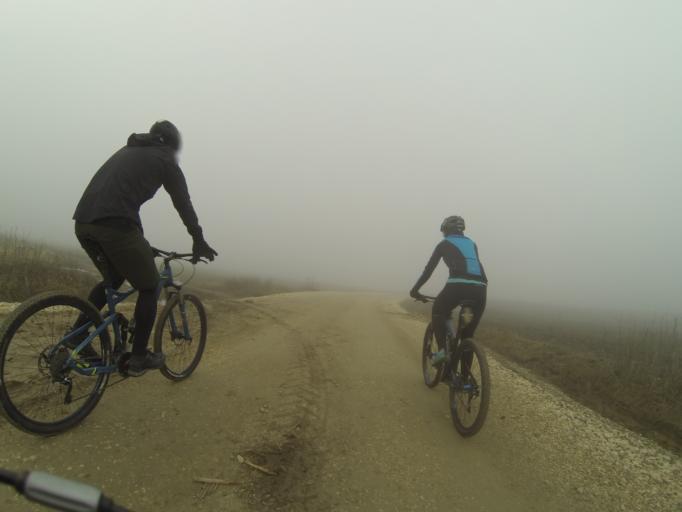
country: RO
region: Mehedinti
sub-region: Comuna Balacita
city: Gvardinita
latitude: 44.4184
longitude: 23.1330
